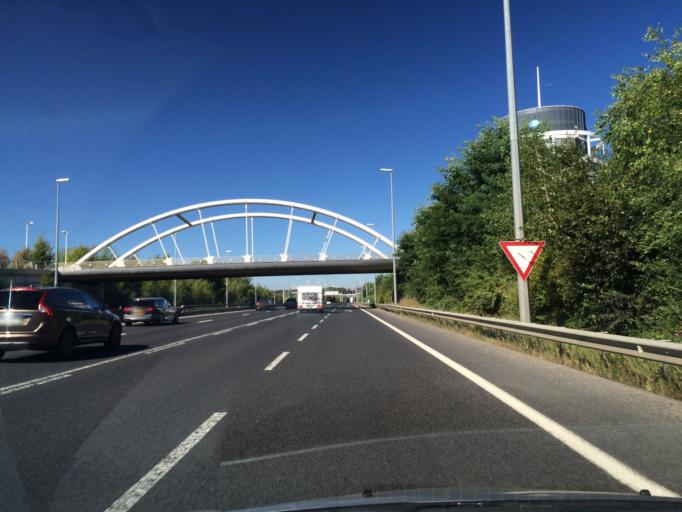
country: LU
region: Luxembourg
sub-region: Canton de Luxembourg
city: Luxembourg
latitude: 49.5783
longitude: 6.1135
